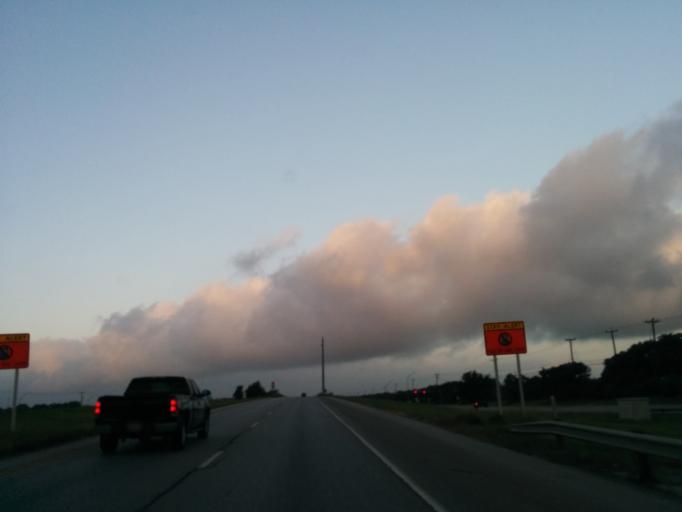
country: US
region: Texas
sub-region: Bexar County
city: Helotes
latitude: 29.5794
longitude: -98.6433
